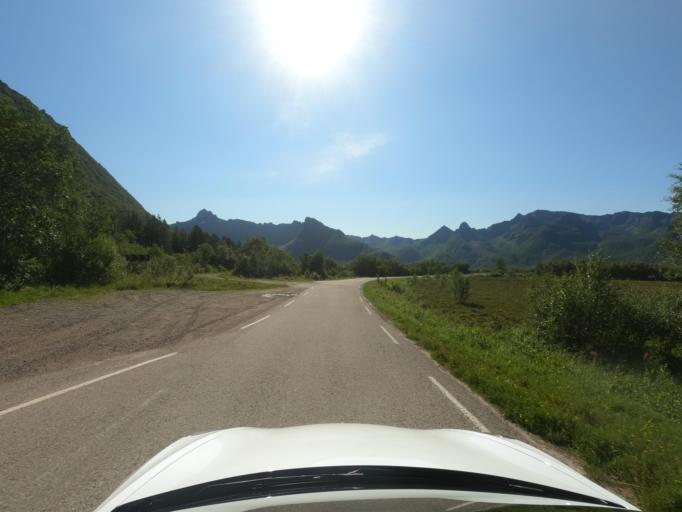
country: NO
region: Nordland
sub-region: Vagan
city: Svolvaer
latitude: 68.4003
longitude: 14.5836
